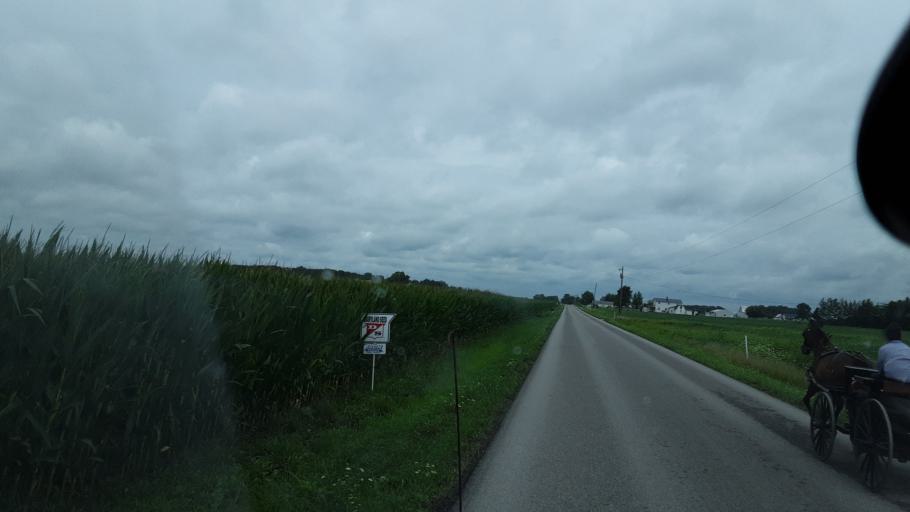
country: US
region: Indiana
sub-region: Adams County
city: Berne
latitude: 40.7230
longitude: -84.9944
